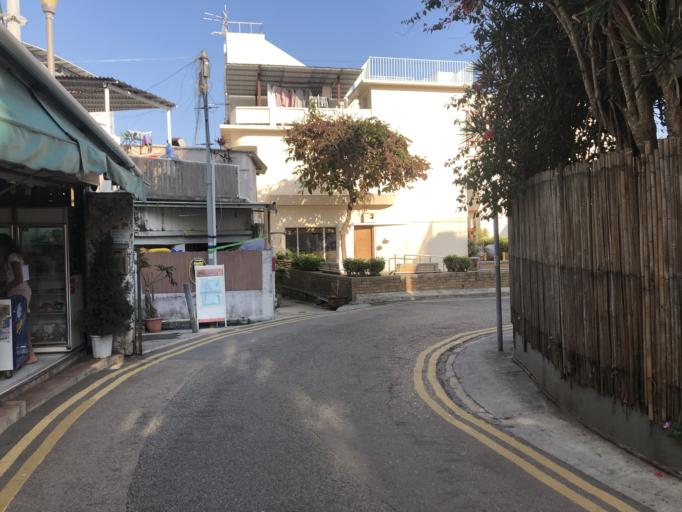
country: HK
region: Wanchai
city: Wan Chai
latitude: 22.2303
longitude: 114.2521
